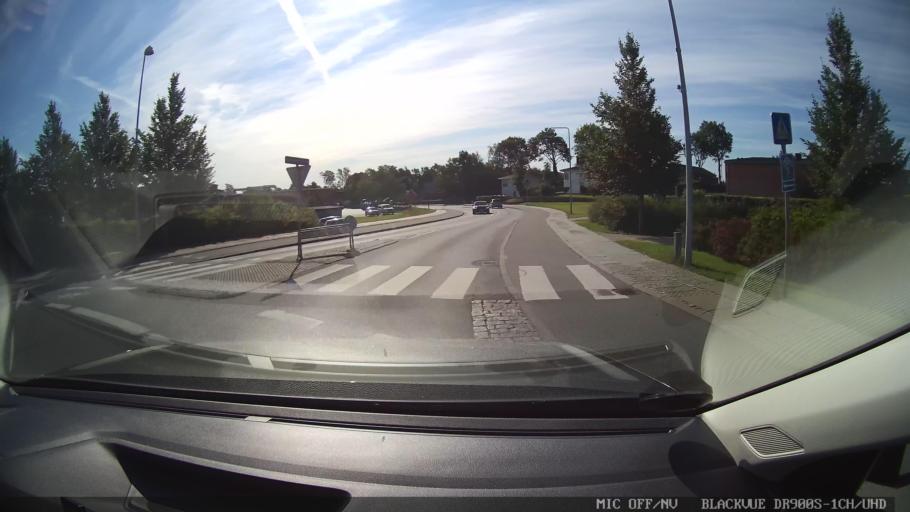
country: DK
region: North Denmark
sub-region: Mariagerfjord Kommune
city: Arden
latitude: 56.7693
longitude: 9.8561
